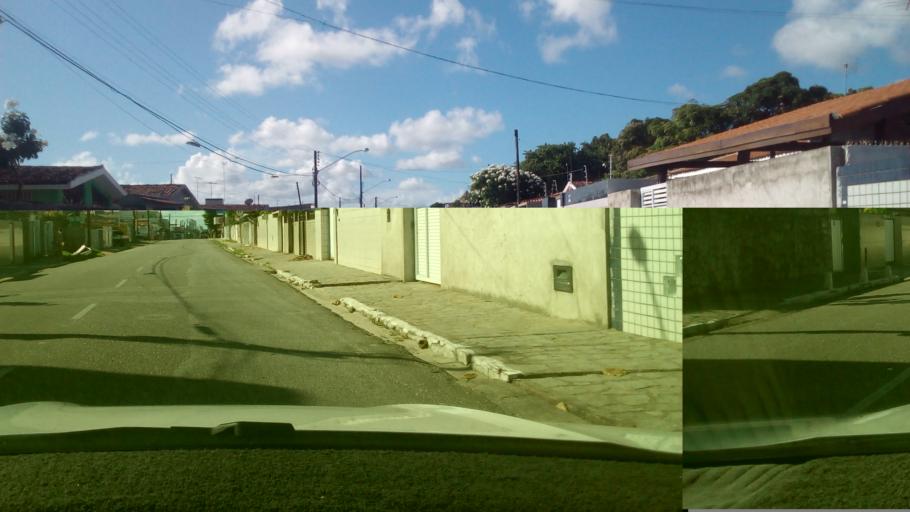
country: BR
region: Paraiba
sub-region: Joao Pessoa
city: Joao Pessoa
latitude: -7.1537
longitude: -34.8723
